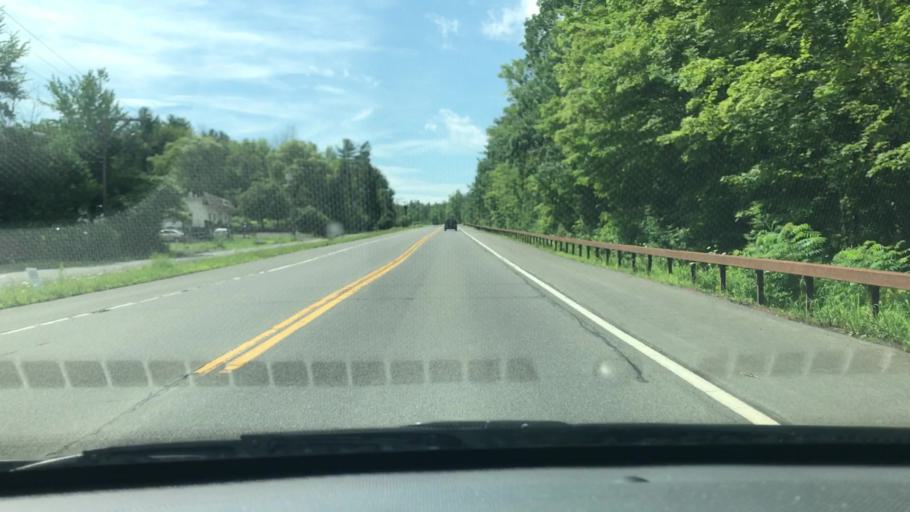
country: US
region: New York
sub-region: Ulster County
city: Shokan
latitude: 41.9984
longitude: -74.2645
